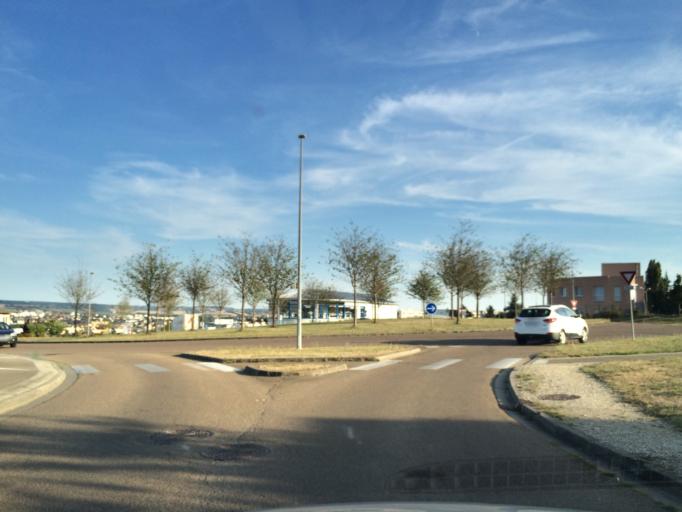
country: FR
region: Bourgogne
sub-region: Departement de l'Yonne
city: Auxerre
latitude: 47.8143
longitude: 3.5663
